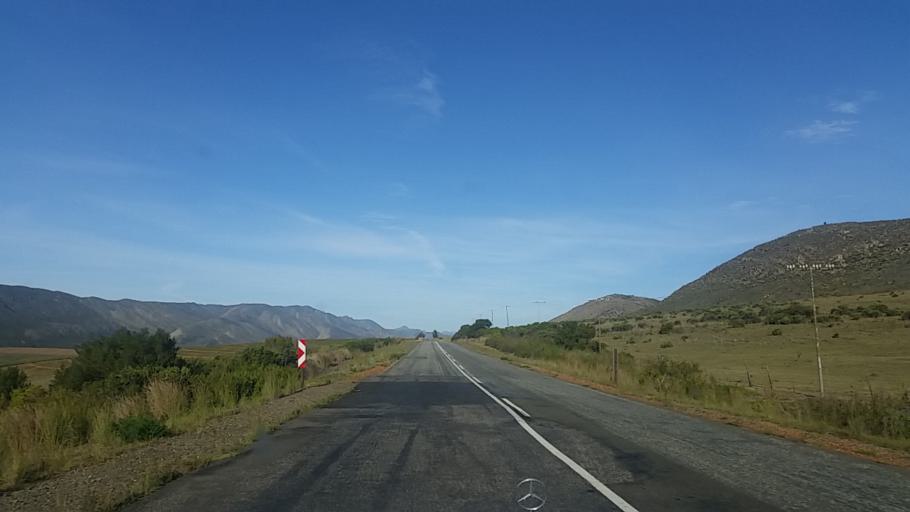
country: ZA
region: Western Cape
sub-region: Eden District Municipality
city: Knysna
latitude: -33.7727
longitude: 22.9309
